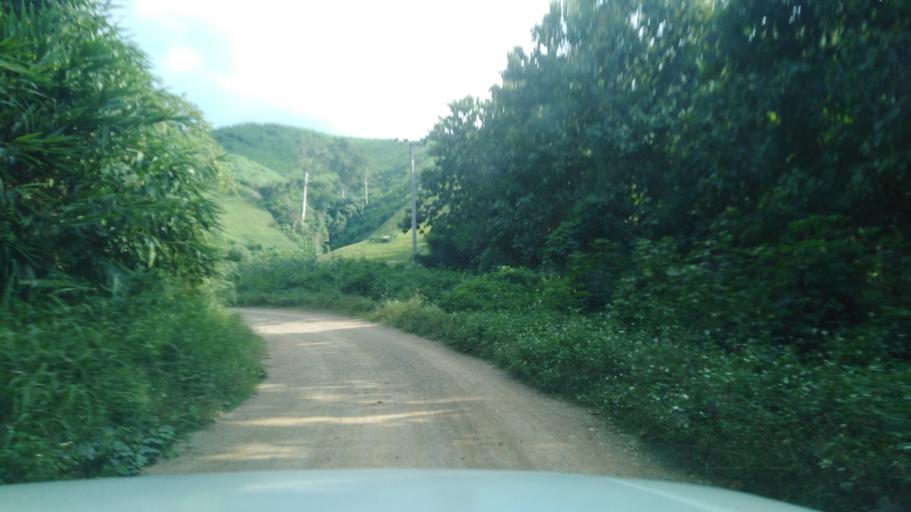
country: TH
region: Chiang Rai
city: Wiang Kaen
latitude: 19.7840
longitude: 100.6300
